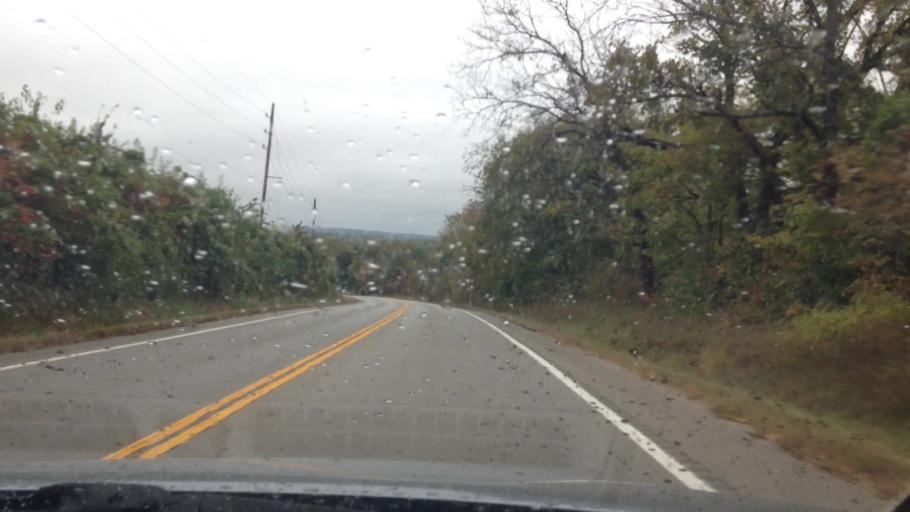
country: US
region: Missouri
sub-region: Platte County
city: Weston
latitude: 39.4078
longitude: -94.8684
